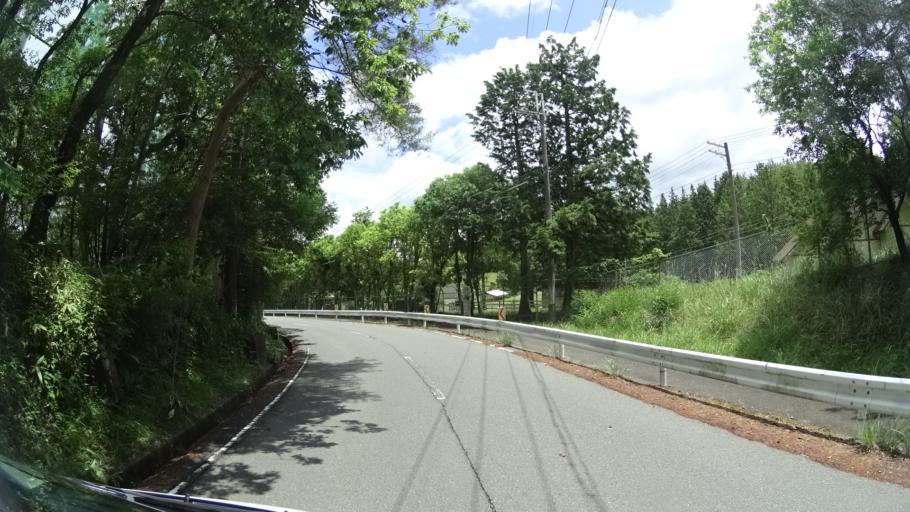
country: JP
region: Hyogo
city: Sasayama
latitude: 35.0288
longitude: 135.3903
